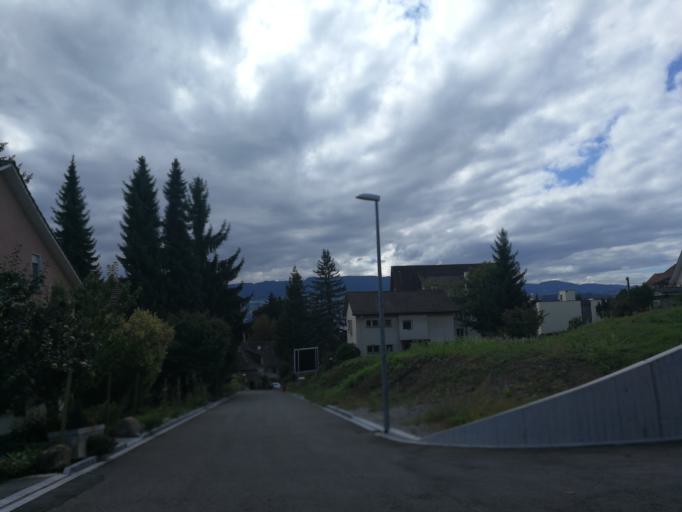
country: CH
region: Zurich
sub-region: Bezirk Meilen
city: Stafa
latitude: 47.2435
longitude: 8.7232
